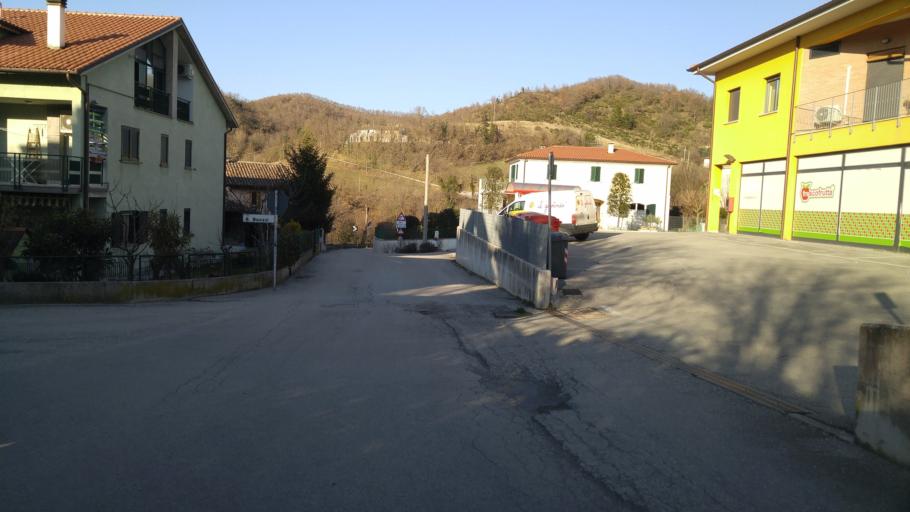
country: IT
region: The Marches
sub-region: Provincia di Pesaro e Urbino
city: Cagli
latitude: 43.5447
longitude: 12.6625
